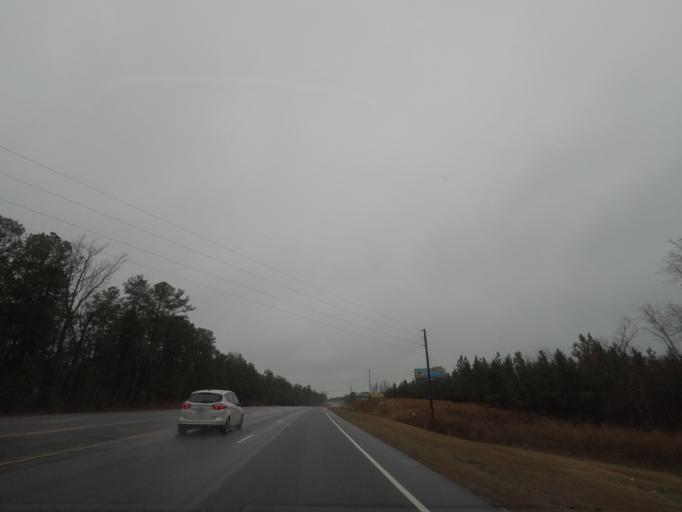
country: US
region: North Carolina
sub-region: Lee County
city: Broadway
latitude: 35.3533
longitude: -79.1091
